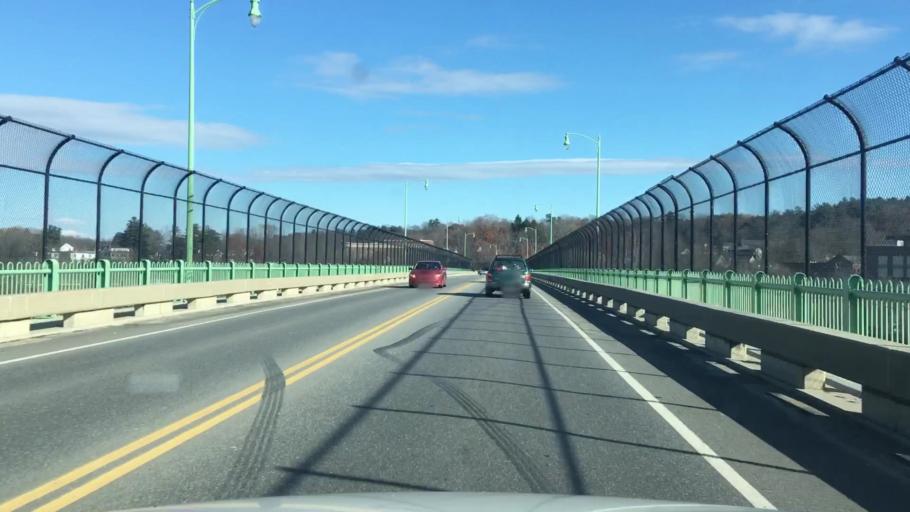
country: US
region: Maine
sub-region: Kennebec County
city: Augusta
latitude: 44.3126
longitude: -69.7724
